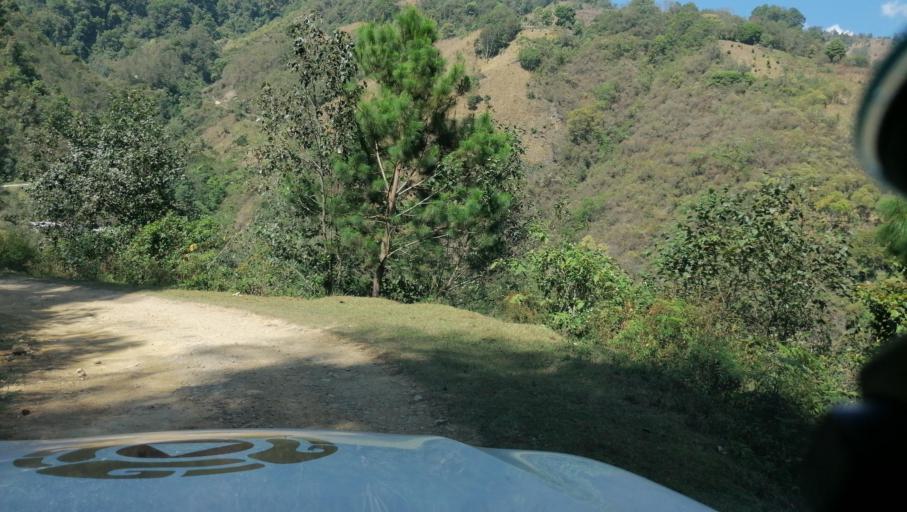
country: GT
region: San Marcos
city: Tacana
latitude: 15.2080
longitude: -92.2099
